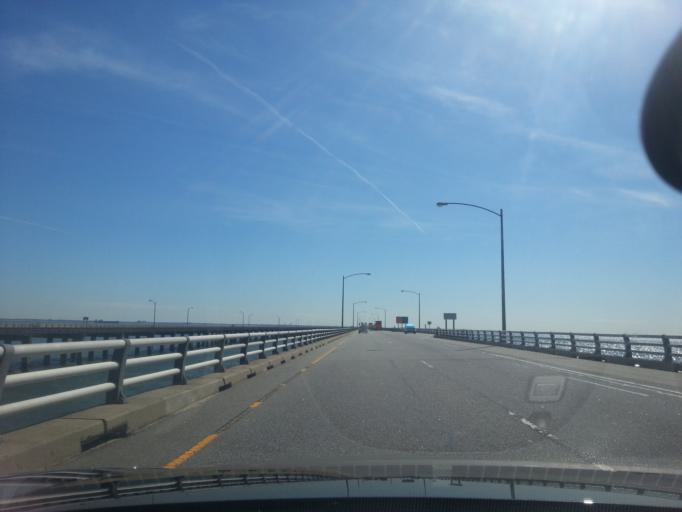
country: US
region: Virginia
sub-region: City of Virginia Beach
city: Virginia Beach
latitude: 37.0112
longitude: -76.0949
